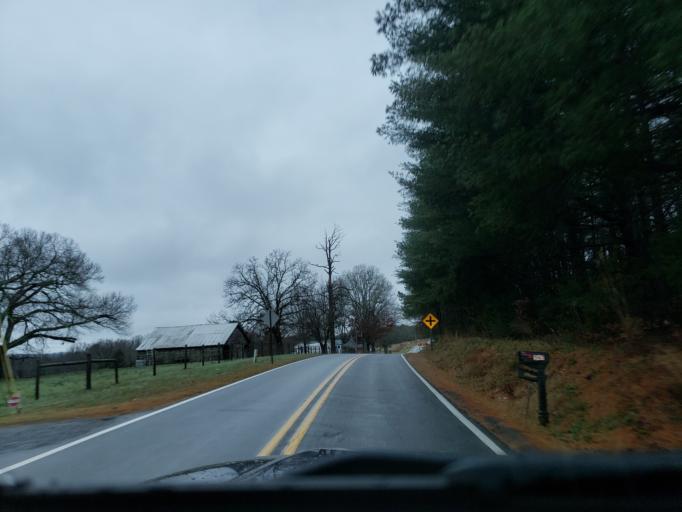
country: US
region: North Carolina
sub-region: Cleveland County
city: White Plains
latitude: 35.1883
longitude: -81.3792
